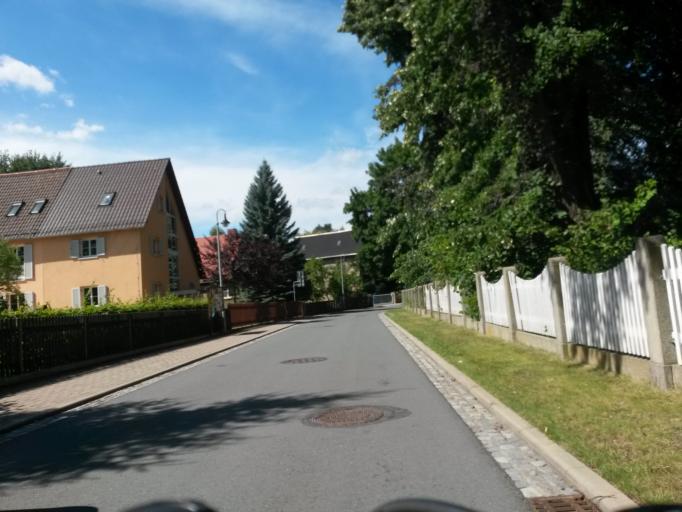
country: DE
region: Thuringia
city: Bad Klosterlausnitz
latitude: 50.9154
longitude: 11.8614
